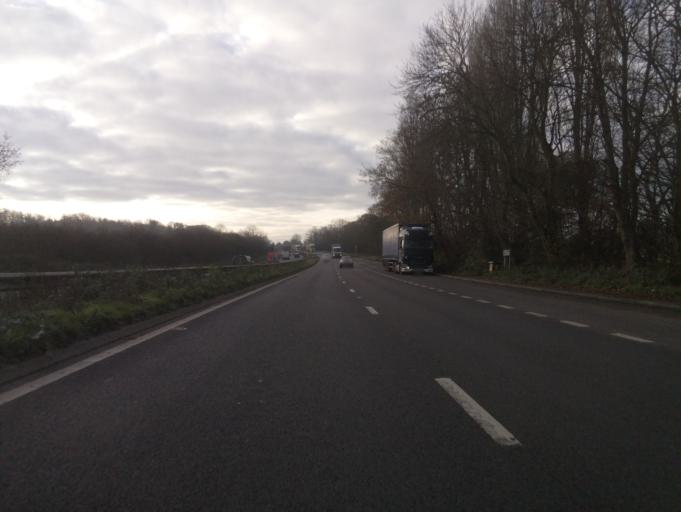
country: GB
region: England
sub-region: Staffordshire
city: Lichfield
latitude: 52.6551
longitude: -1.8099
